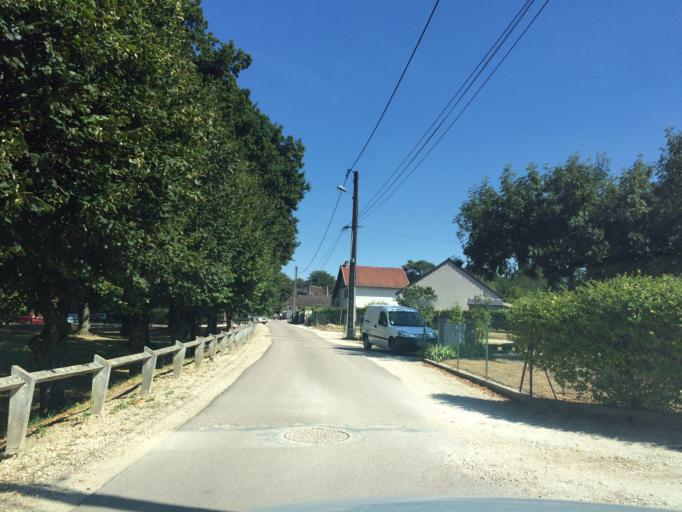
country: FR
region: Bourgogne
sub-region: Departement de l'Yonne
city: Cheny
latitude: 47.9235
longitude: 3.5209
